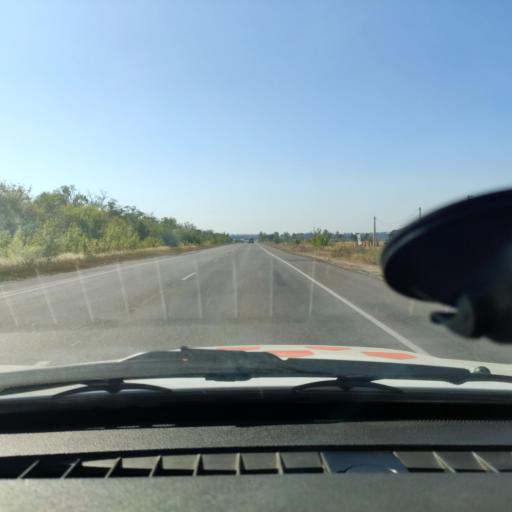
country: RU
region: Voronezj
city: Novaya Usman'
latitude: 51.6145
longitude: 39.3365
